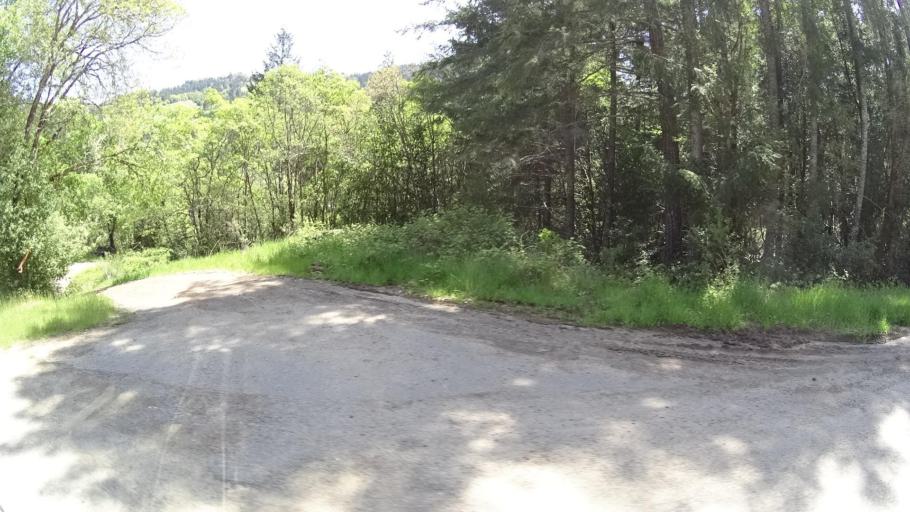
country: US
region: California
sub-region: Humboldt County
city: Redway
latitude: 40.2021
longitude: -123.5247
